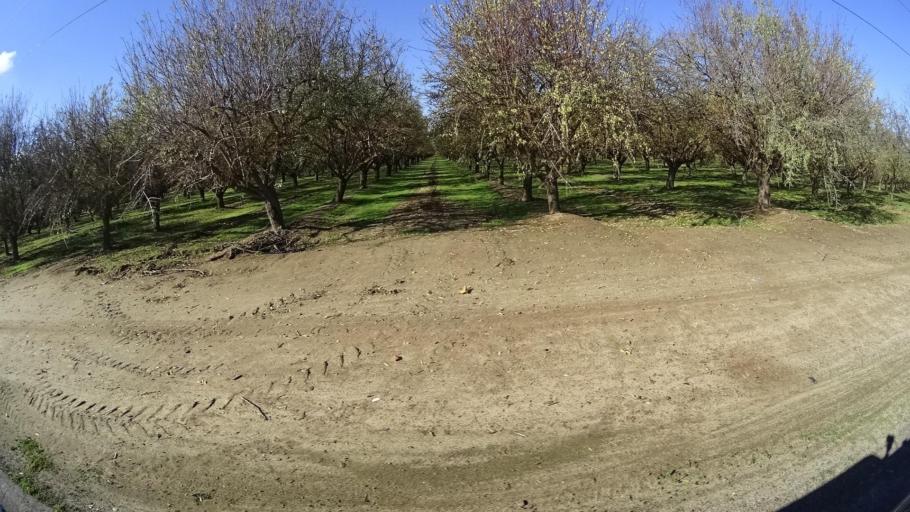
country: US
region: California
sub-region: Kern County
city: Delano
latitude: 35.7235
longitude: -119.2585
